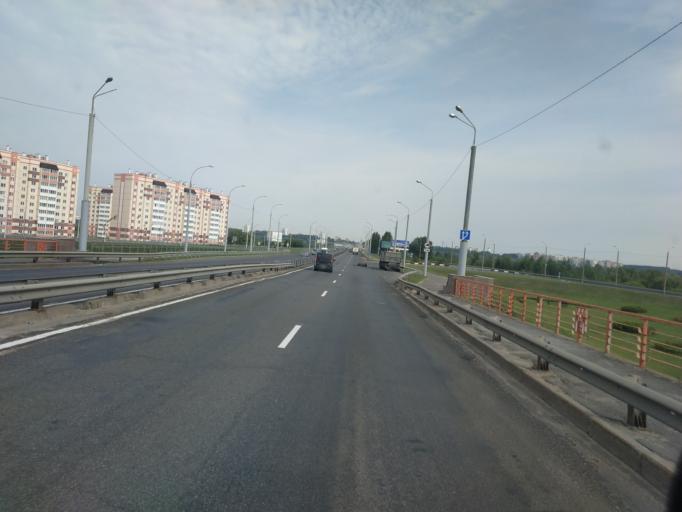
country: BY
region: Mogilev
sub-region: Mahilyowski Rayon
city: Veyno
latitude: 53.8826
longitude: 30.3812
